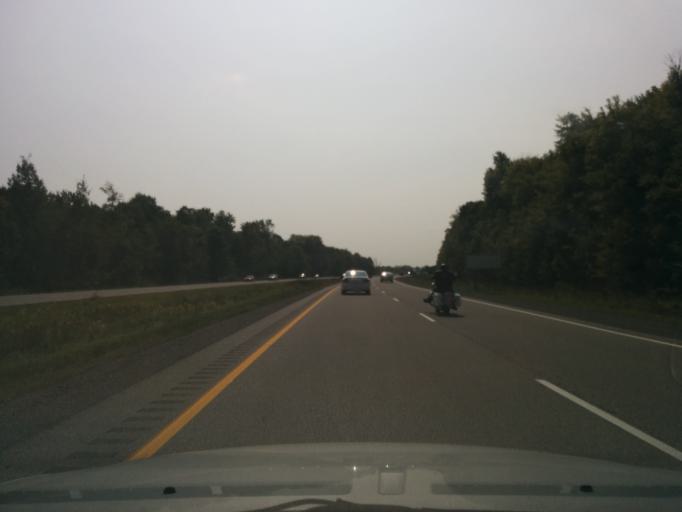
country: CA
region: Ontario
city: Bells Corners
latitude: 45.1617
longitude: -75.6879
